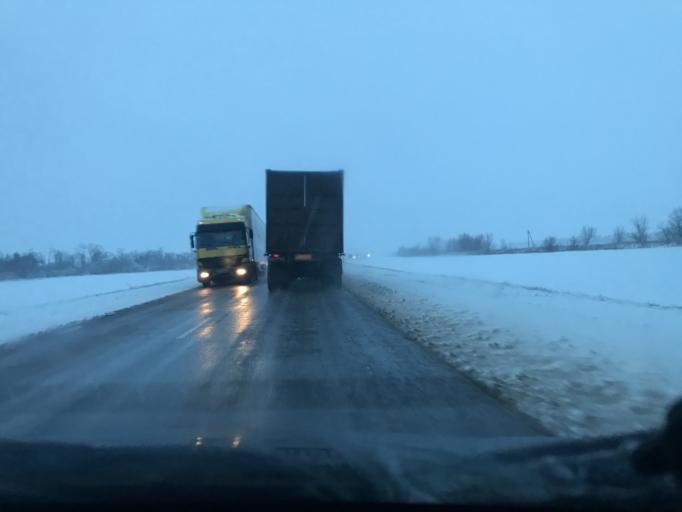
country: RU
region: Rostov
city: Letnik
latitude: 46.0548
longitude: 41.2105
